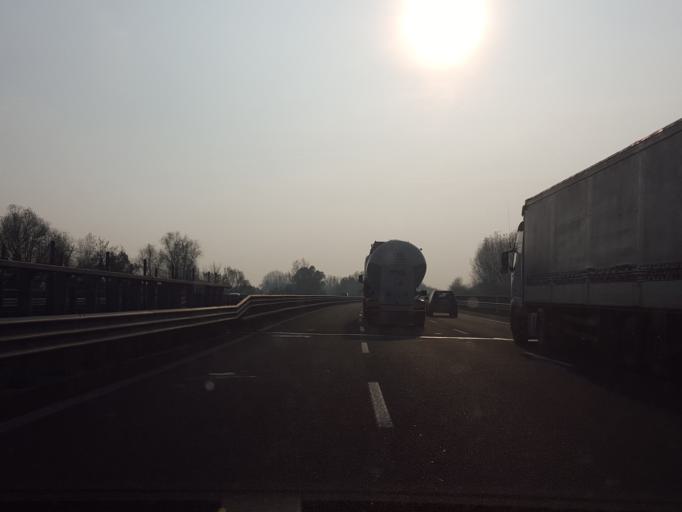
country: IT
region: Veneto
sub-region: Provincia di Treviso
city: Cendon
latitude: 45.6361
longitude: 12.3126
